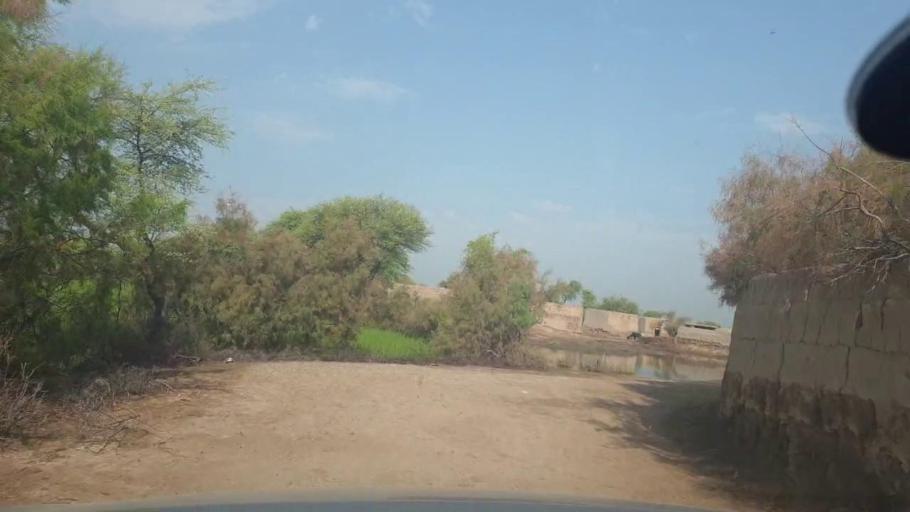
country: PK
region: Balochistan
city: Mehrabpur
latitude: 28.0737
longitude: 68.2106
